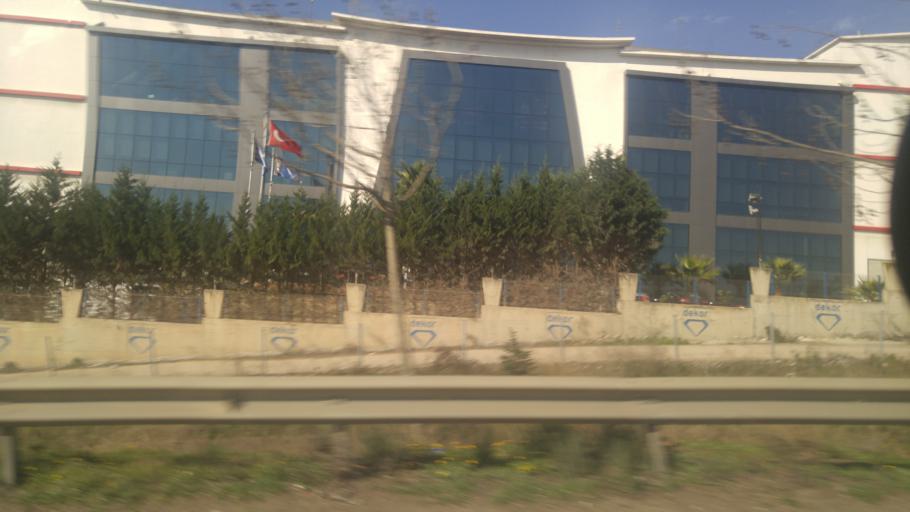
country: TR
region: Kocaeli
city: Balcik
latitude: 40.8542
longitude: 29.3751
